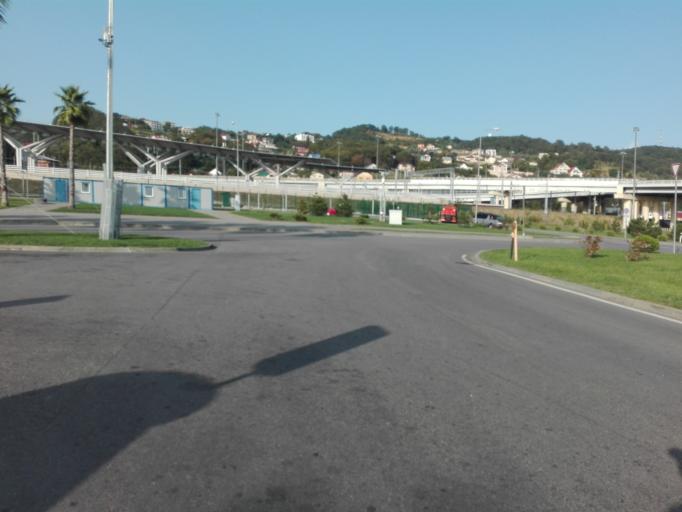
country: RU
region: Krasnodarskiy
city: Vysokoye
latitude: 43.4100
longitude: 39.9751
